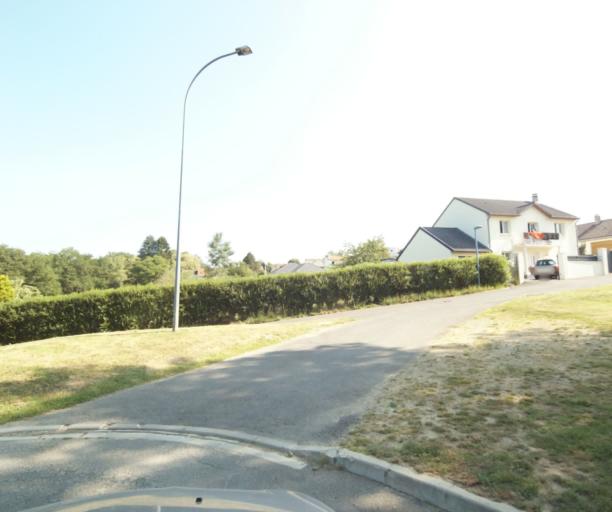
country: FR
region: Champagne-Ardenne
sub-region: Departement des Ardennes
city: Charleville-Mezieres
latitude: 49.7842
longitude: 4.7080
